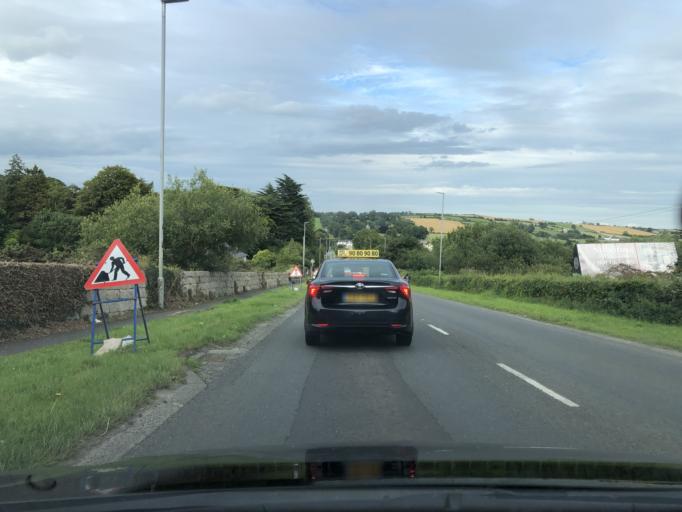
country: GB
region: Northern Ireland
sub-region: Down District
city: Castlewellan
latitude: 54.2613
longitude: -5.9311
